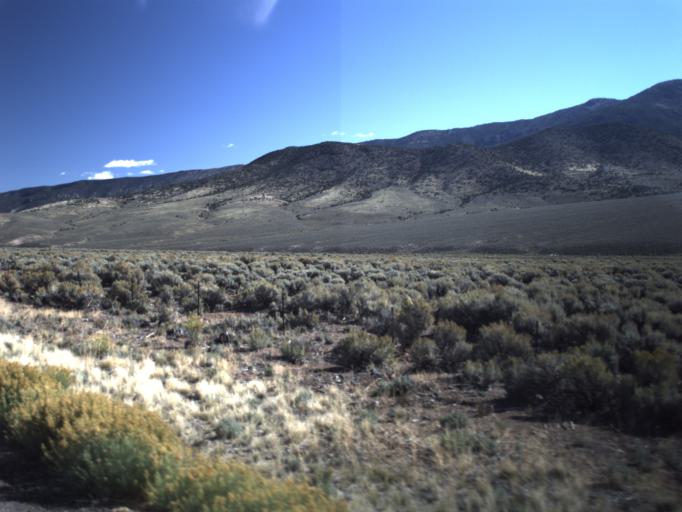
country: US
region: Utah
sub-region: Piute County
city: Junction
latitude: 38.3299
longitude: -111.9586
